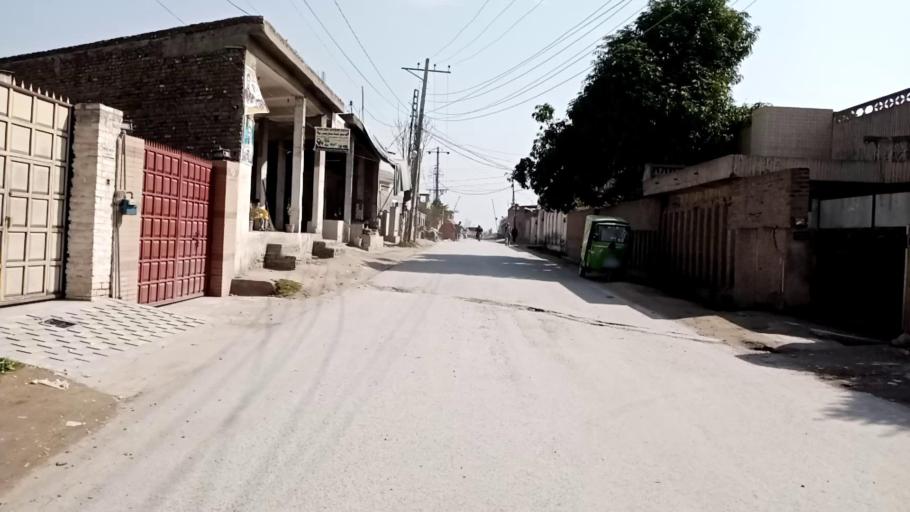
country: PK
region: Khyber Pakhtunkhwa
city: Peshawar
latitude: 33.9947
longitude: 71.5075
